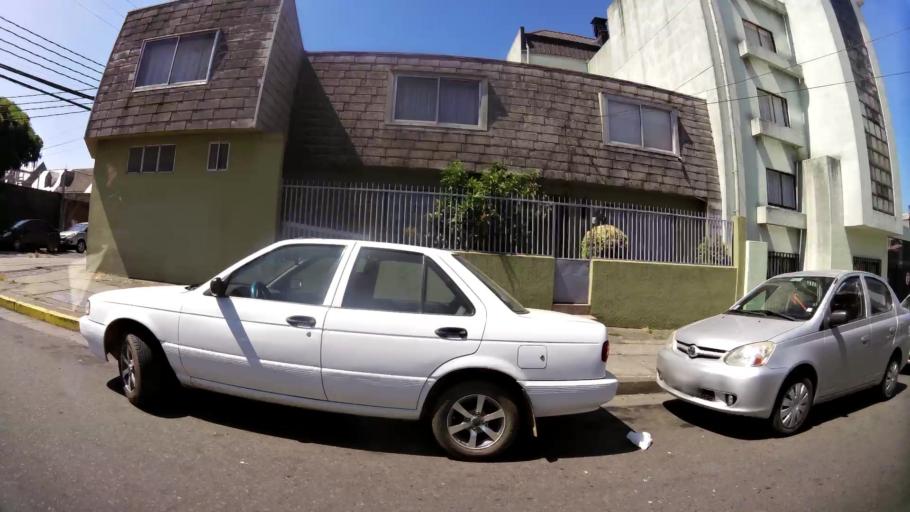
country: CL
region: Biobio
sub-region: Provincia de Concepcion
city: Concepcion
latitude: -36.8208
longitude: -73.0519
